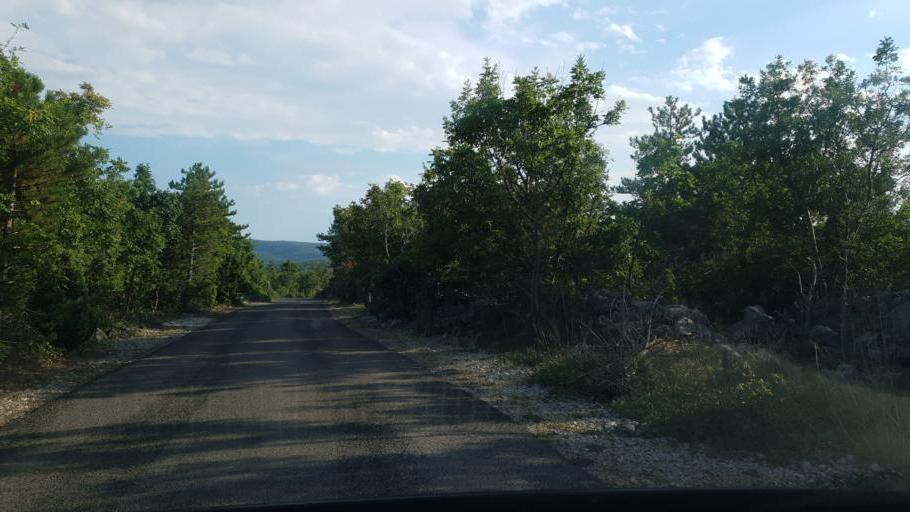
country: HR
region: Primorsko-Goranska
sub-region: Grad Crikvenica
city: Jadranovo
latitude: 45.1789
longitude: 14.6075
